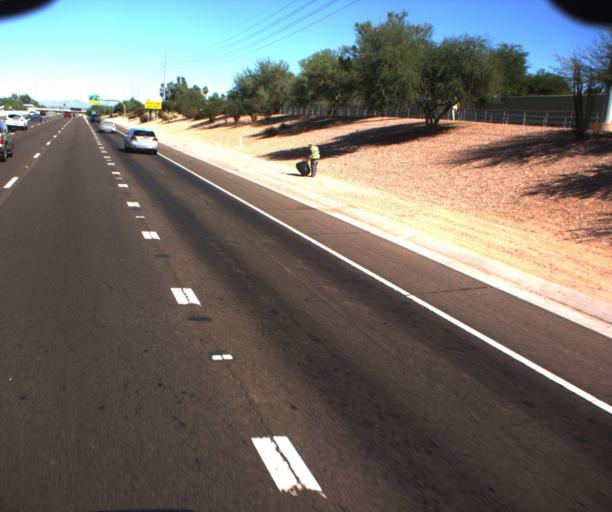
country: US
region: Arizona
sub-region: Maricopa County
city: Paradise Valley
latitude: 33.5903
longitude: -111.8914
